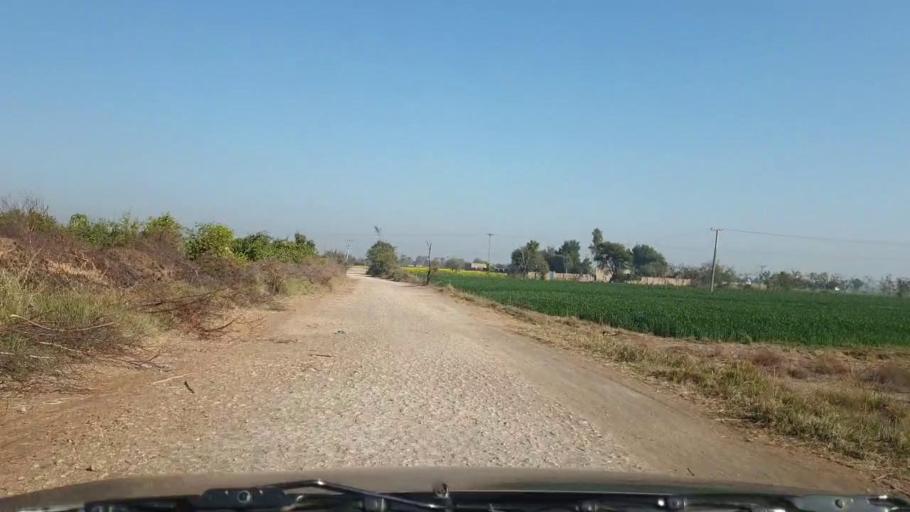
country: PK
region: Sindh
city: Jhol
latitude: 25.9437
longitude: 68.8377
